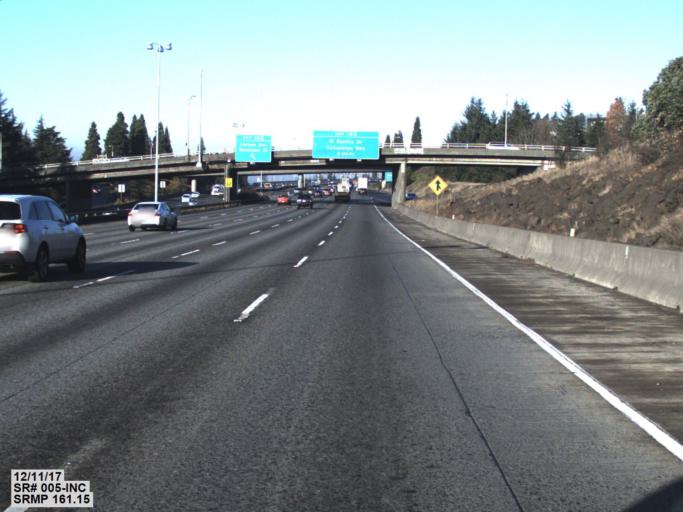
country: US
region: Washington
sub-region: King County
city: White Center
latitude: 47.5480
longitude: -122.3108
